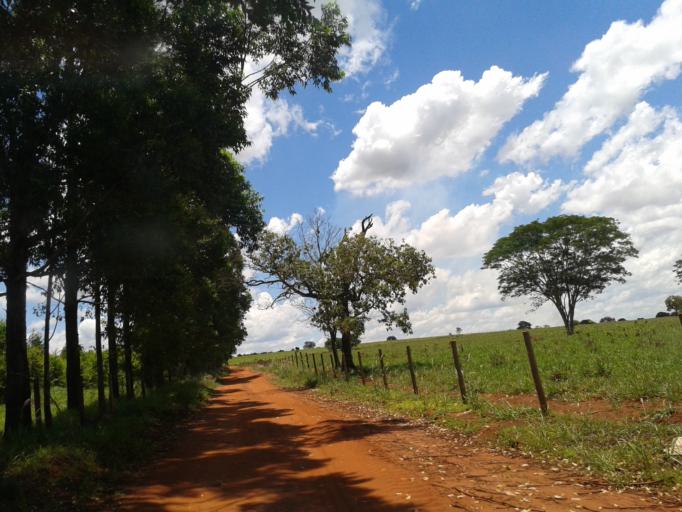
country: BR
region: Minas Gerais
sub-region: Centralina
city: Centralina
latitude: -18.7027
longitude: -49.1709
